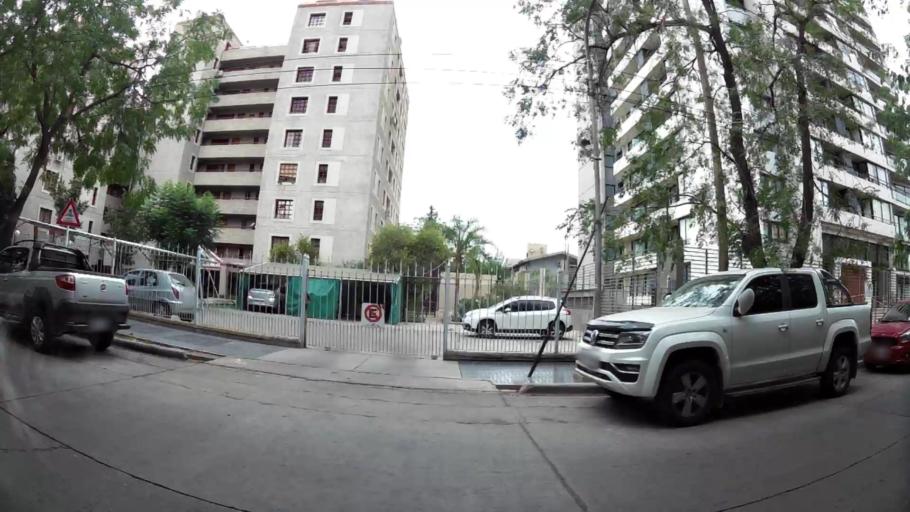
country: AR
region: Mendoza
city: Mendoza
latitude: -32.8748
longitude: -68.8444
